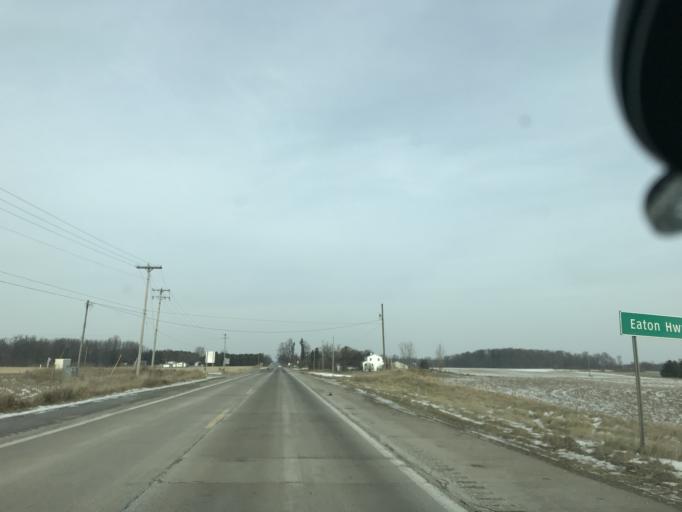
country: US
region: Michigan
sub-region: Ionia County
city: Lake Odessa
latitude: 42.7692
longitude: -85.0742
